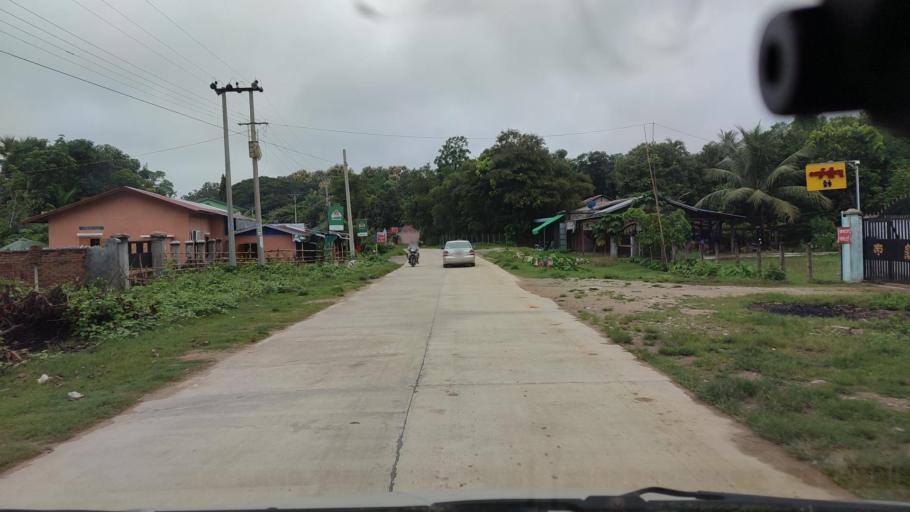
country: MM
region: Bago
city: Taungoo
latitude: 18.9718
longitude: 96.5018
